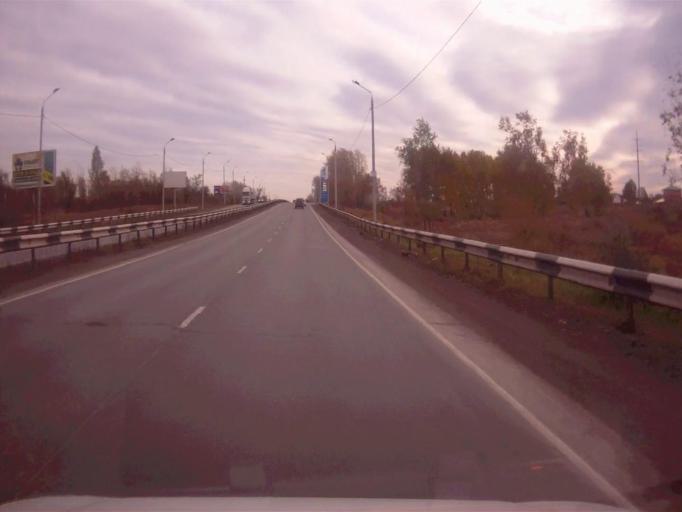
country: RU
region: Chelyabinsk
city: Novosineglazovskiy
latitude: 55.0580
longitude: 61.4046
